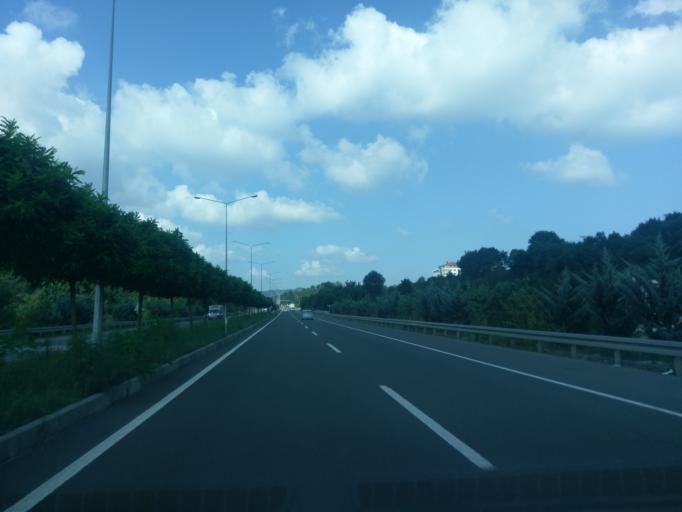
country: TR
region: Ordu
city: Unieh
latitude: 41.1147
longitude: 37.3061
